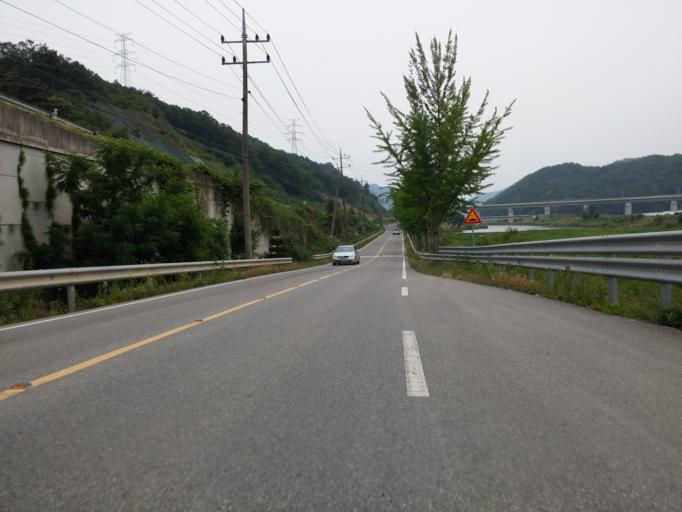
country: KR
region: Chungcheongbuk-do
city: Okcheon
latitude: 36.2913
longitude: 127.5295
